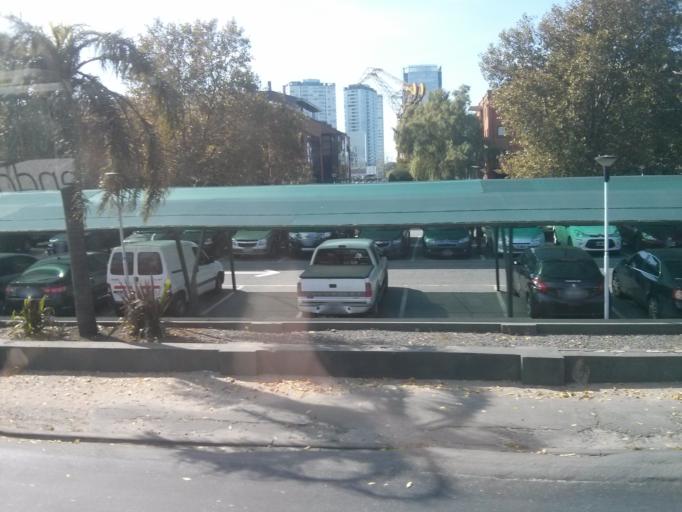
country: AR
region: Buenos Aires F.D.
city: Buenos Aires
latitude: -34.6198
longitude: -58.3662
